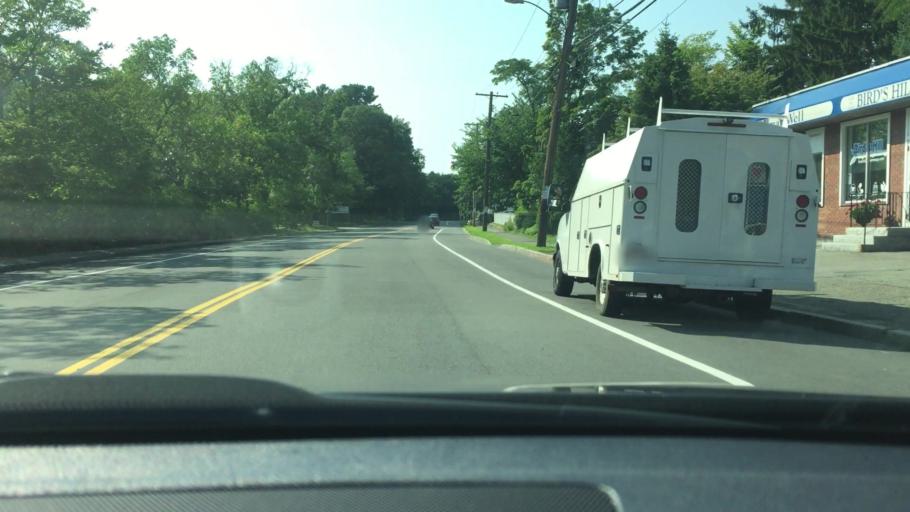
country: US
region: Massachusetts
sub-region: Norfolk County
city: Needham
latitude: 42.2760
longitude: -71.2152
